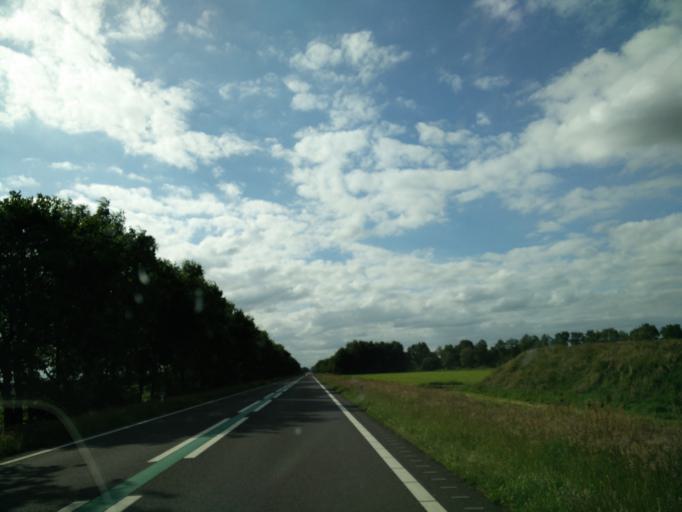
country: NL
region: Drenthe
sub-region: Gemeente Assen
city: Assen
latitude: 52.8456
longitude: 6.5769
